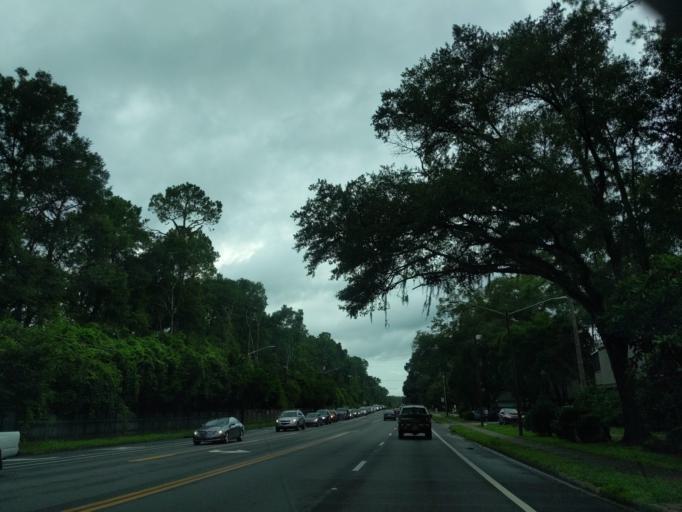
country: US
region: Florida
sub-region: Alachua County
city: Gainesville
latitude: 29.6457
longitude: -82.4224
